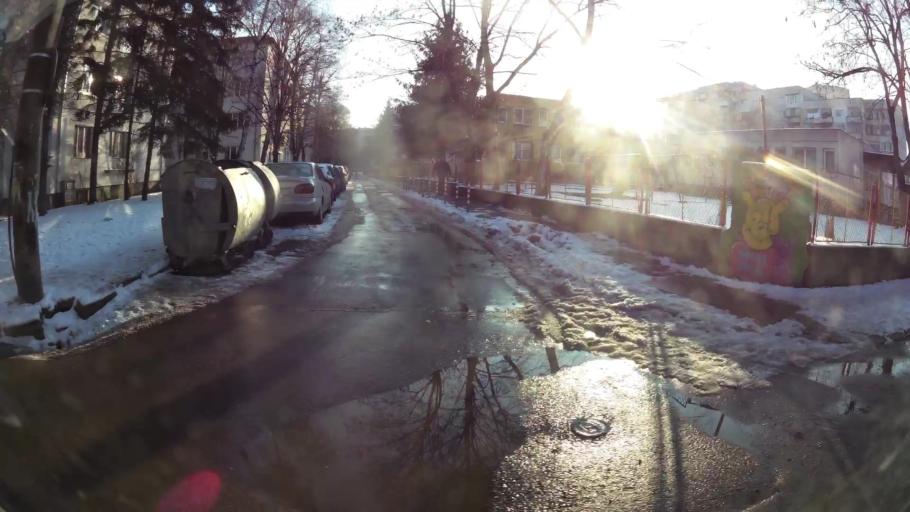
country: BG
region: Sofia-Capital
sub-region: Stolichna Obshtina
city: Sofia
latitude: 42.6836
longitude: 23.3577
